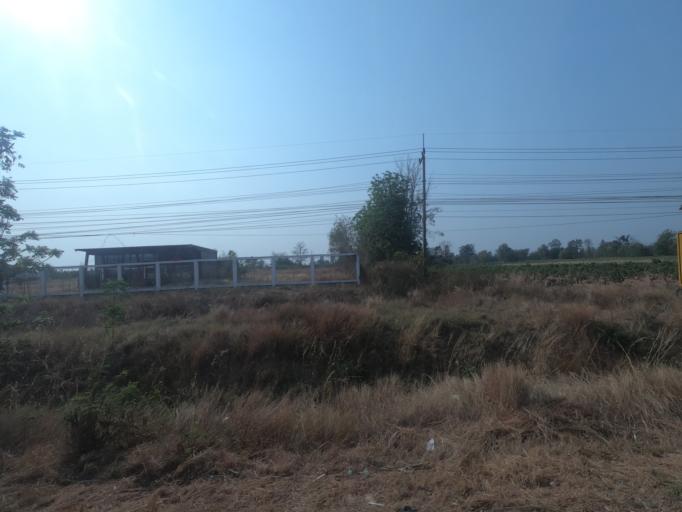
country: TH
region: Khon Kaen
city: Ban Haet
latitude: 16.1710
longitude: 102.7551
